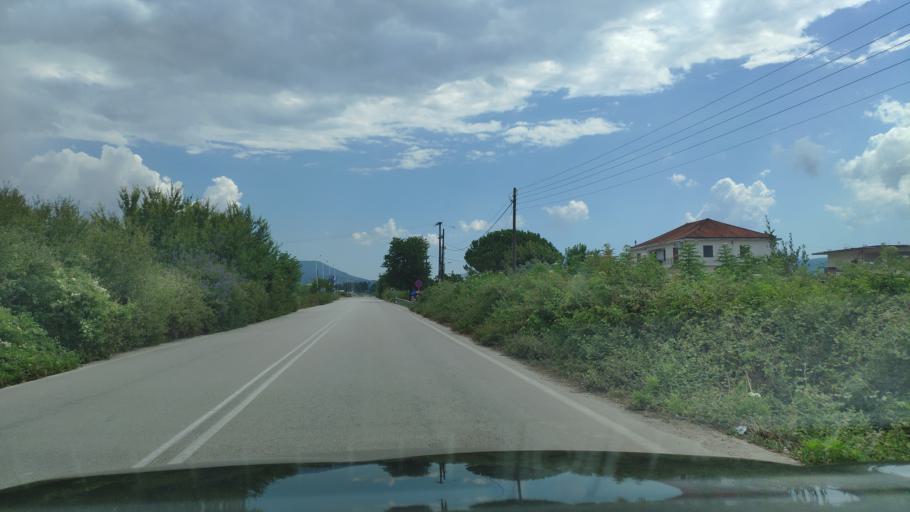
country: GR
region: West Greece
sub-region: Nomos Aitolias kai Akarnanias
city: Krikellos
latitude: 38.9353
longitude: 21.1771
